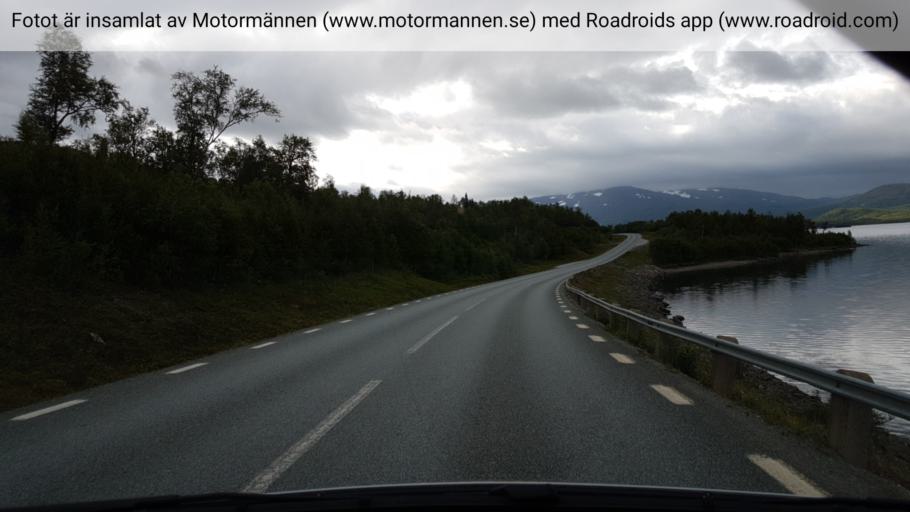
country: NO
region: Nordland
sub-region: Rana
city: Mo i Rana
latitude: 66.0904
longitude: 14.8591
